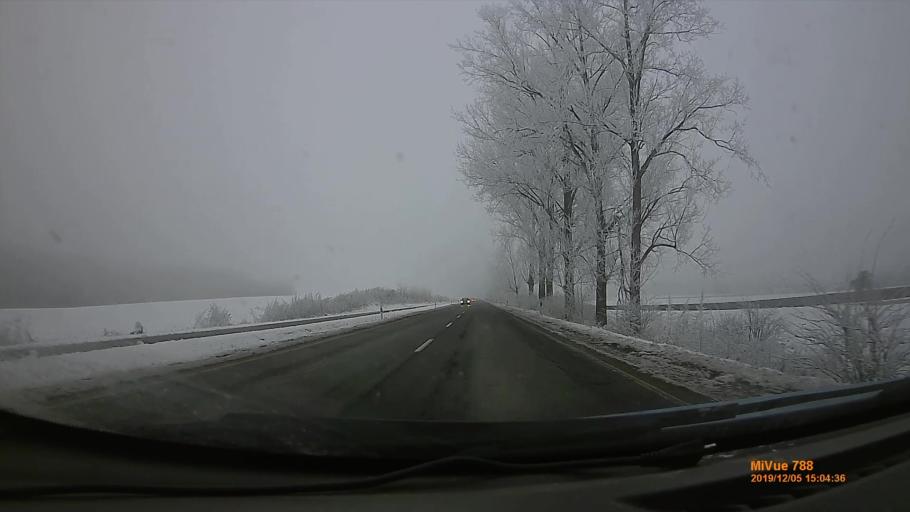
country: HU
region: Szabolcs-Szatmar-Bereg
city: Tiszanagyfalu
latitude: 48.0990
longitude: 21.4920
